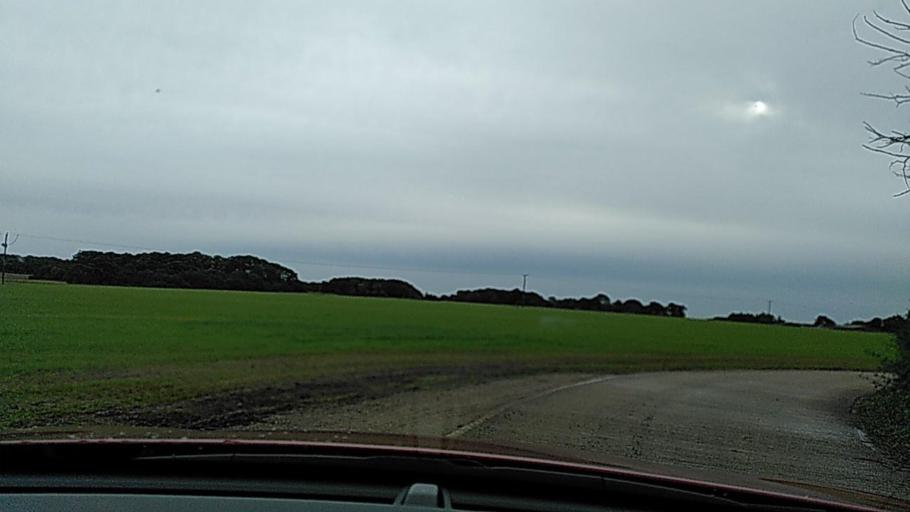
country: GB
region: England
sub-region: West Berkshire
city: Tilehurst
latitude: 51.4875
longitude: -1.0224
